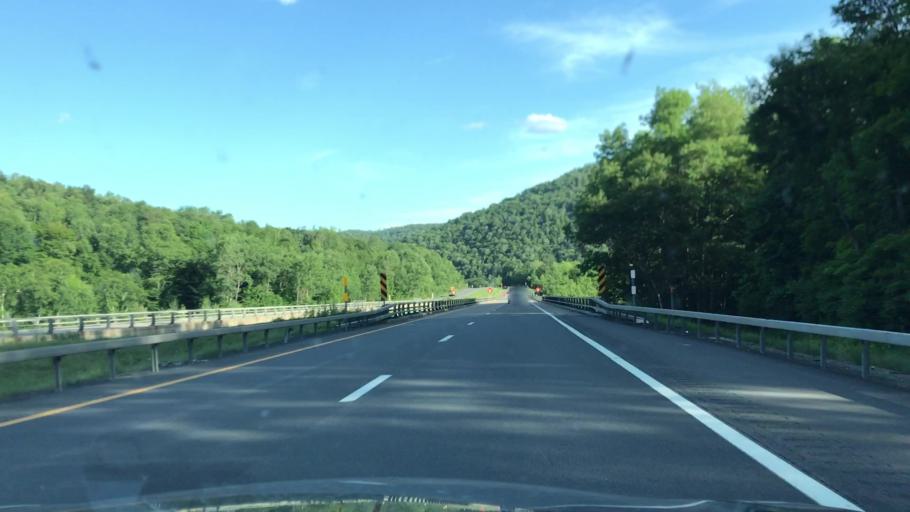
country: US
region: New York
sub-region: Delaware County
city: Walton
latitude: 41.9785
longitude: -75.0544
